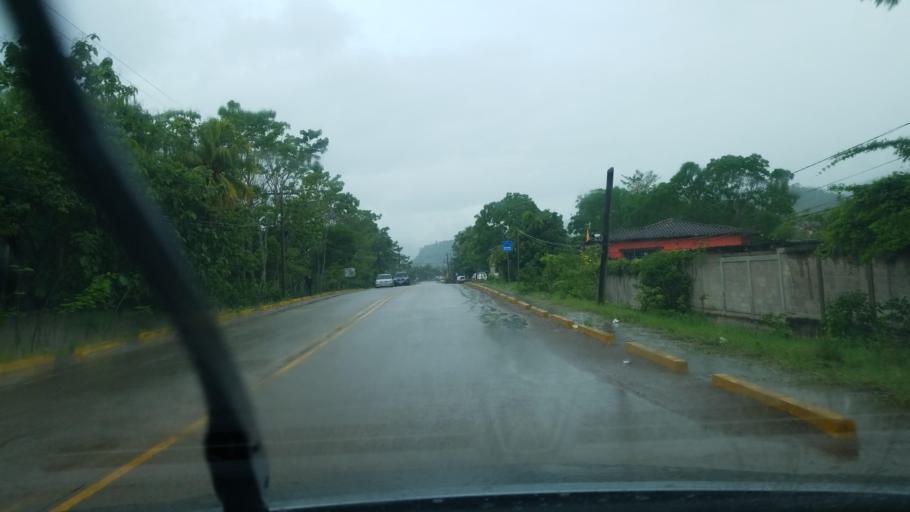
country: HN
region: Copan
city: Copan
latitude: 14.8351
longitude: -89.1538
